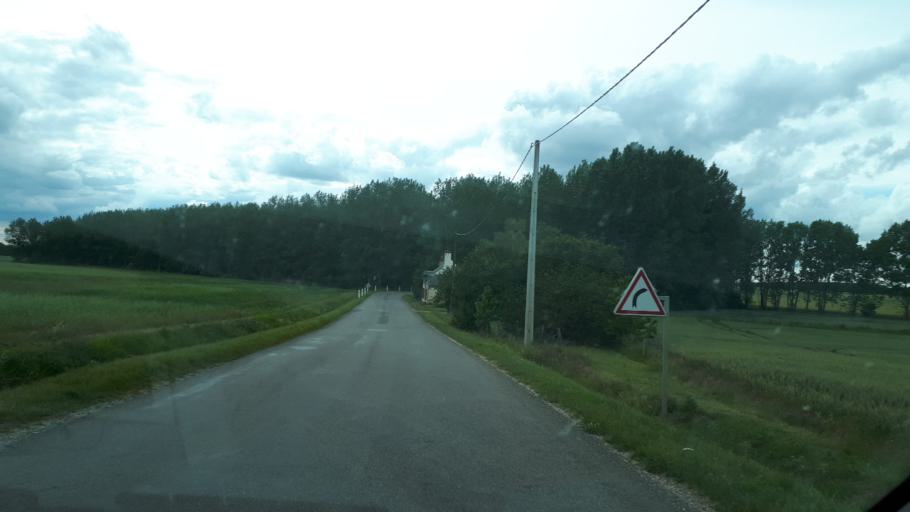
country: FR
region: Centre
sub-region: Departement du Cher
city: Massay
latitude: 47.0967
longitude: 1.9858
